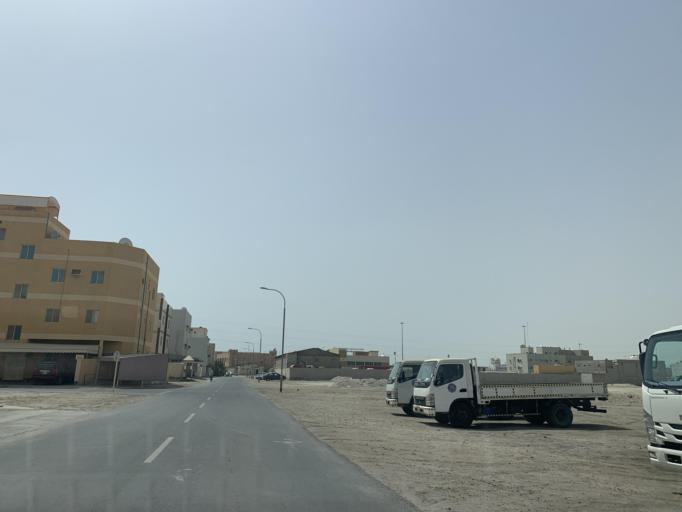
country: BH
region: Northern
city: Sitrah
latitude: 26.1361
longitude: 50.6026
